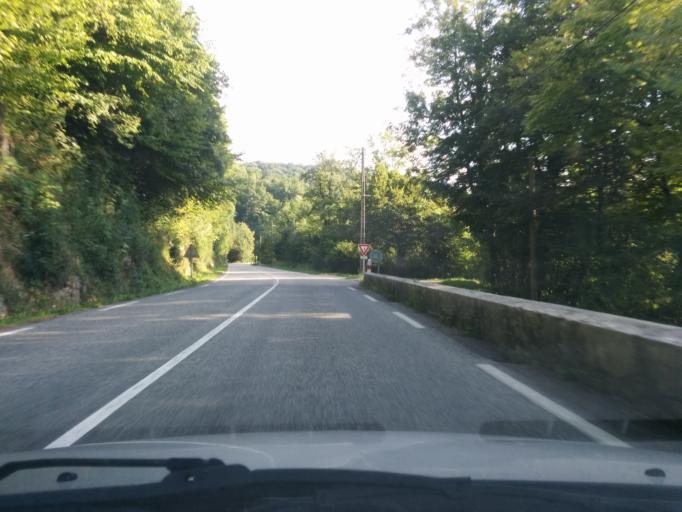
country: FR
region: Rhone-Alpes
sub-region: Departement de la Savoie
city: Saint-Beron
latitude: 45.4875
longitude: 5.7213
